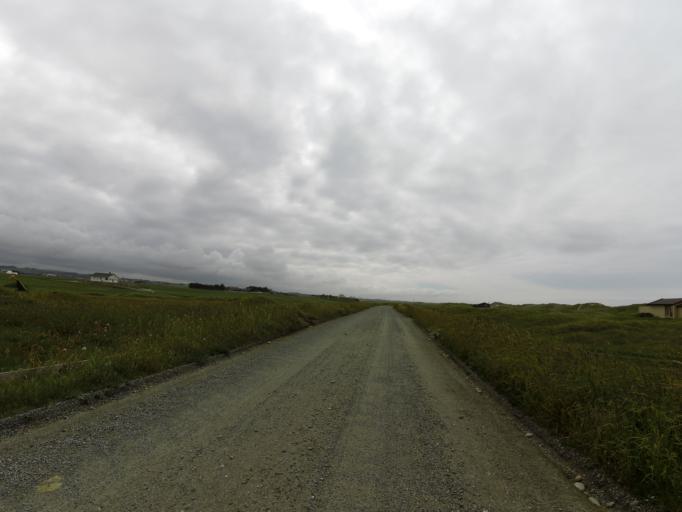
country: NO
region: Rogaland
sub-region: Klepp
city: Kleppe
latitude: 58.8082
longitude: 5.5509
